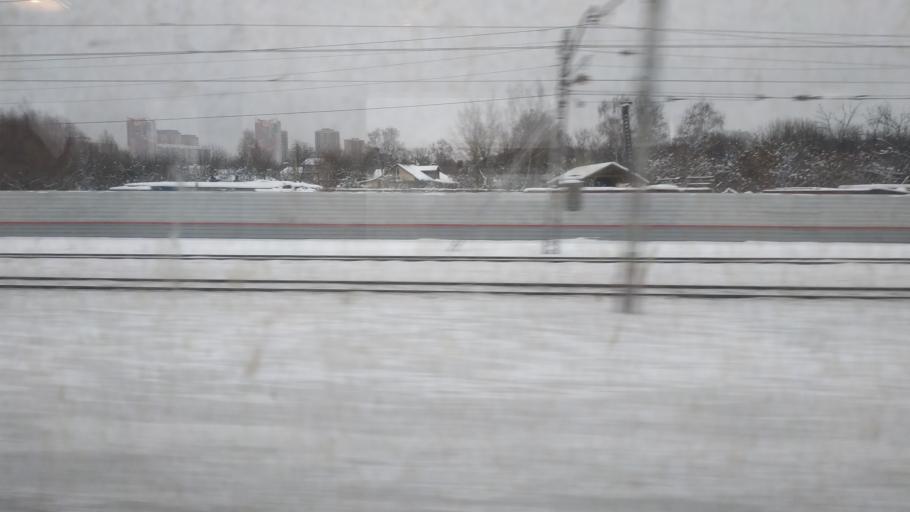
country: RU
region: Moscow
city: Annino
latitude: 55.5453
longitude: 37.5722
